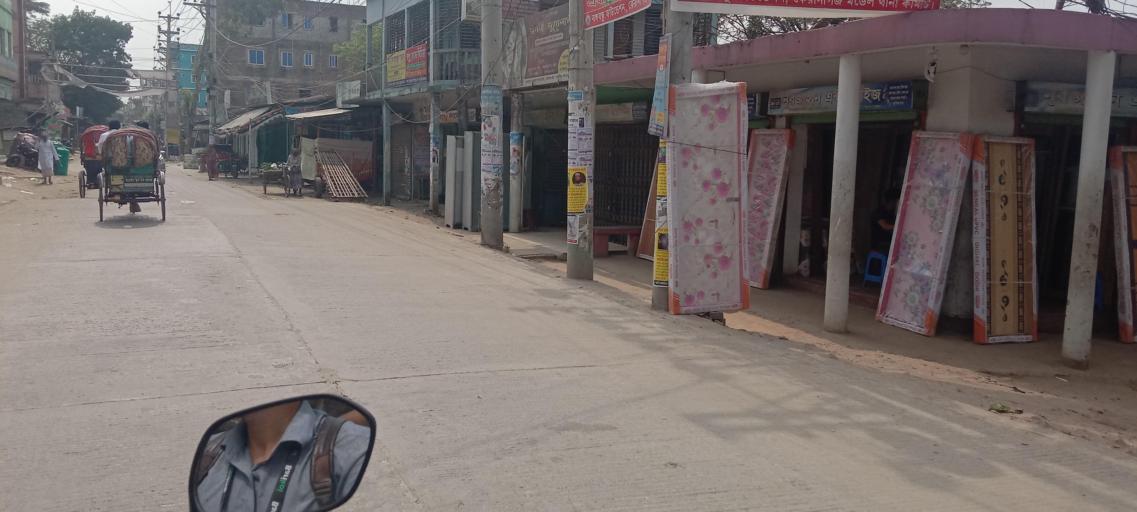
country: BD
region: Dhaka
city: Azimpur
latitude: 23.7137
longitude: 90.3562
